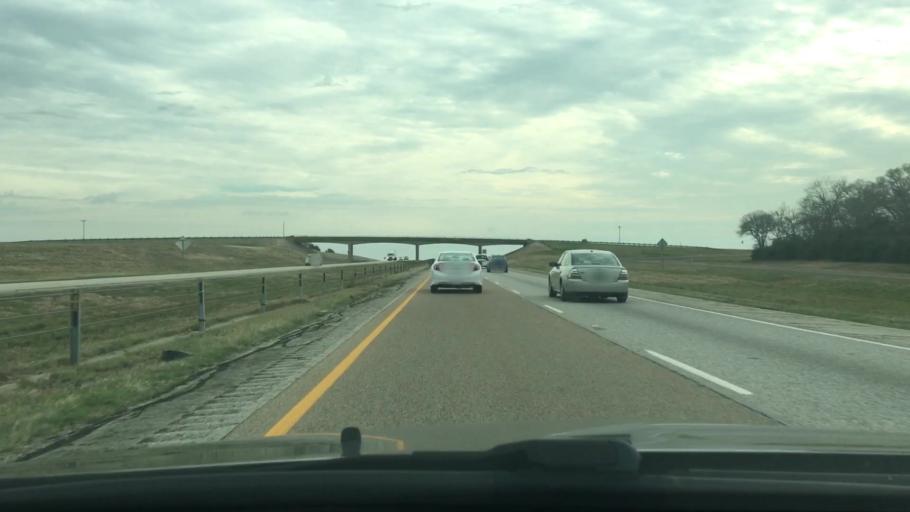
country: US
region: Texas
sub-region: Leon County
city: Centerville
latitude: 31.1266
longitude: -95.9769
